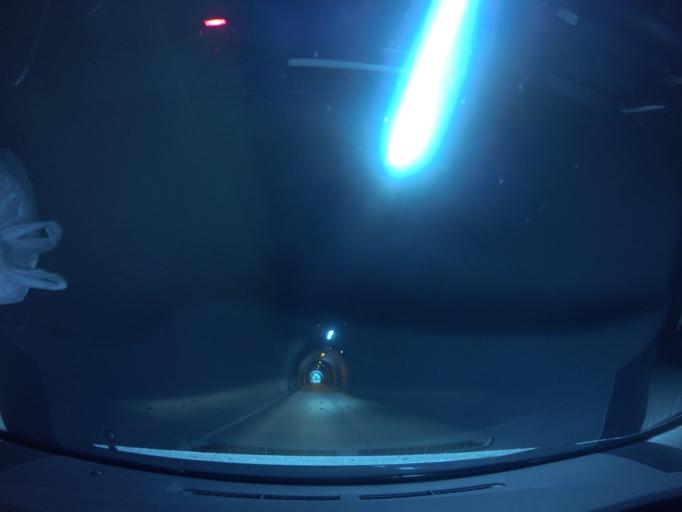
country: JP
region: Wakayama
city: Koya
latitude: 34.0543
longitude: 135.7680
